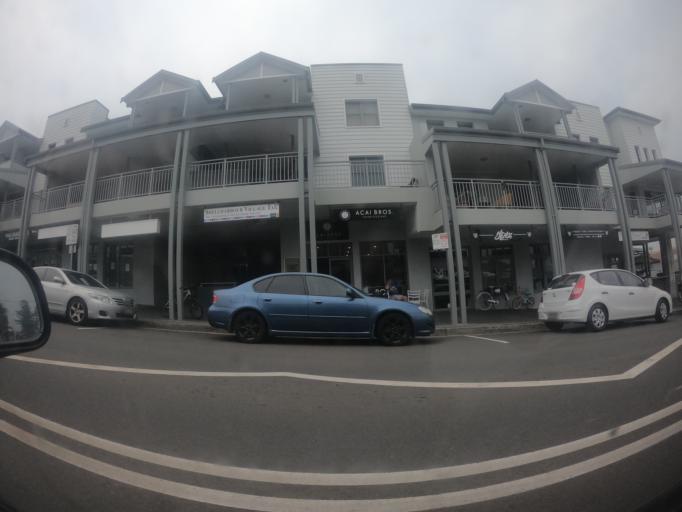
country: AU
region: New South Wales
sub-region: Shellharbour
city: Shellharbour Village
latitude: -34.5793
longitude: 150.8670
